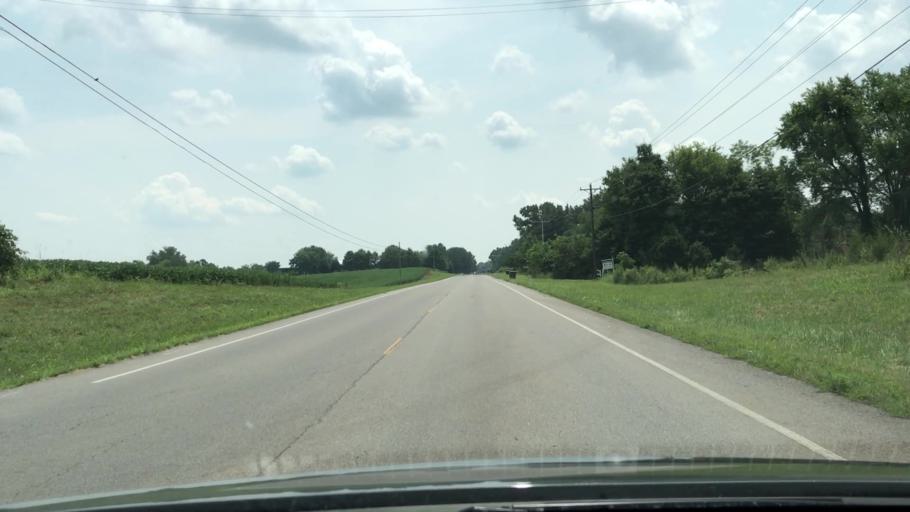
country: US
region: Tennessee
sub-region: Sumner County
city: Portland
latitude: 36.5339
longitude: -86.5035
